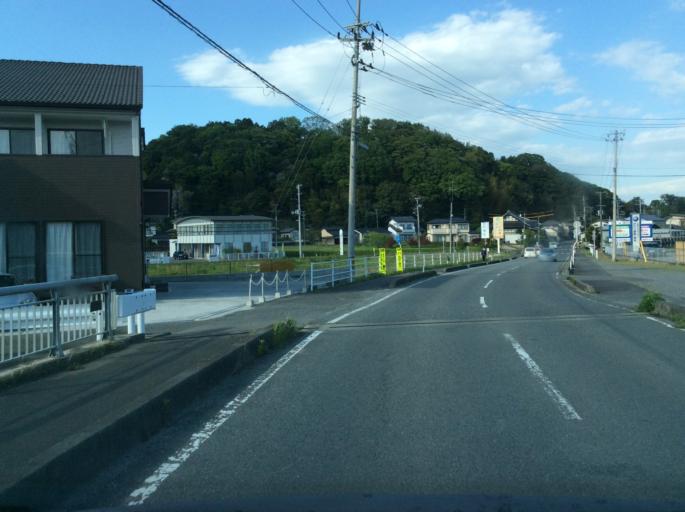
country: JP
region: Fukushima
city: Iwaki
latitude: 36.9853
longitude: 140.8461
